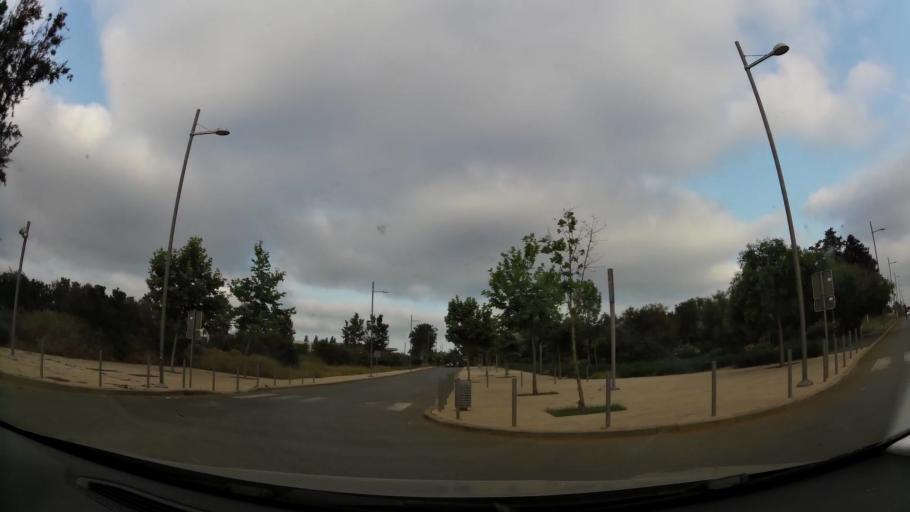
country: MA
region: Rabat-Sale-Zemmour-Zaer
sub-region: Rabat
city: Rabat
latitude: 33.9485
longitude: -6.8326
